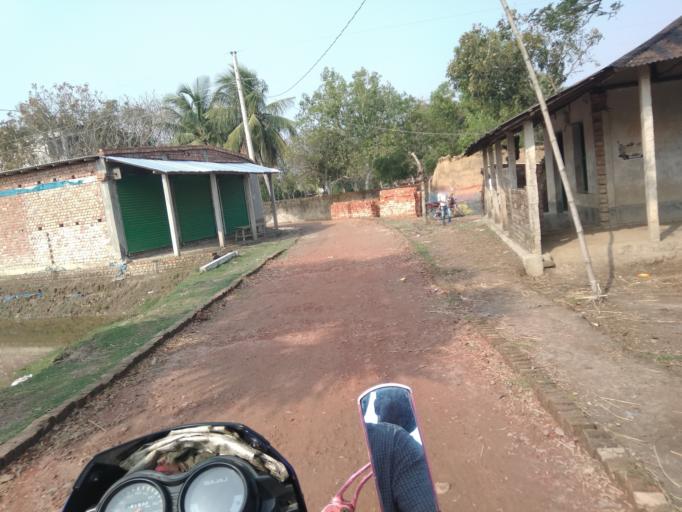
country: IN
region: West Bengal
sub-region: North 24 Parganas
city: Gosaba
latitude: 22.2648
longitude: 89.1159
